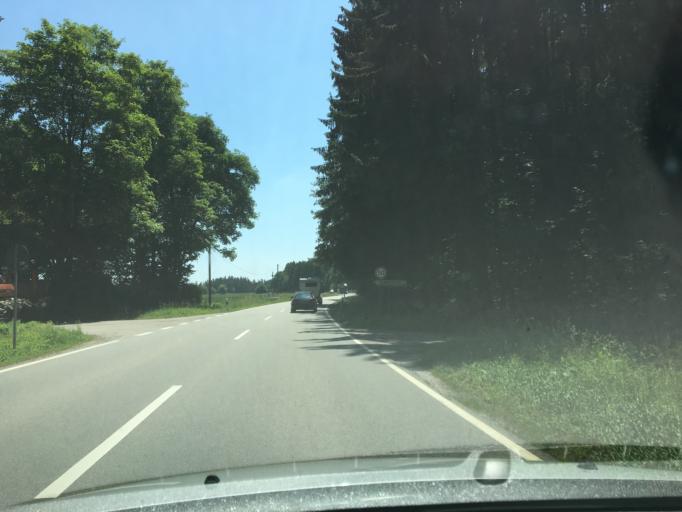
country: DE
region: Bavaria
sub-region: Upper Bavaria
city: Niedertaufkirchen
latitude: 48.3343
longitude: 12.5234
